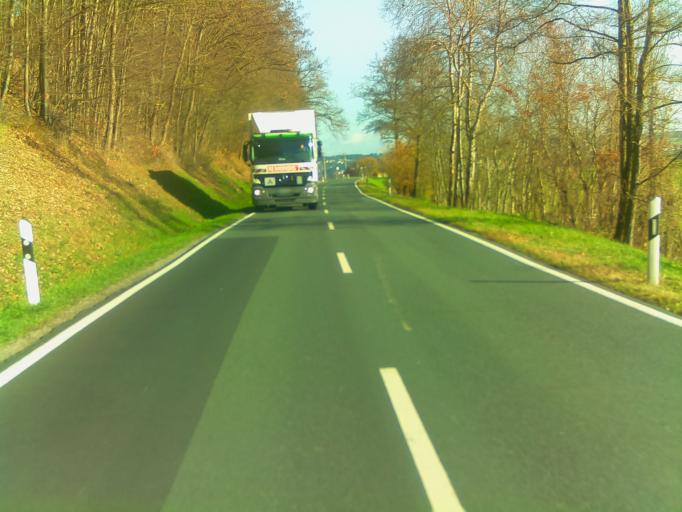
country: DE
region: Bavaria
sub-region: Regierungsbezirk Unterfranken
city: Hohenroth
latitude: 50.3018
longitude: 10.1722
